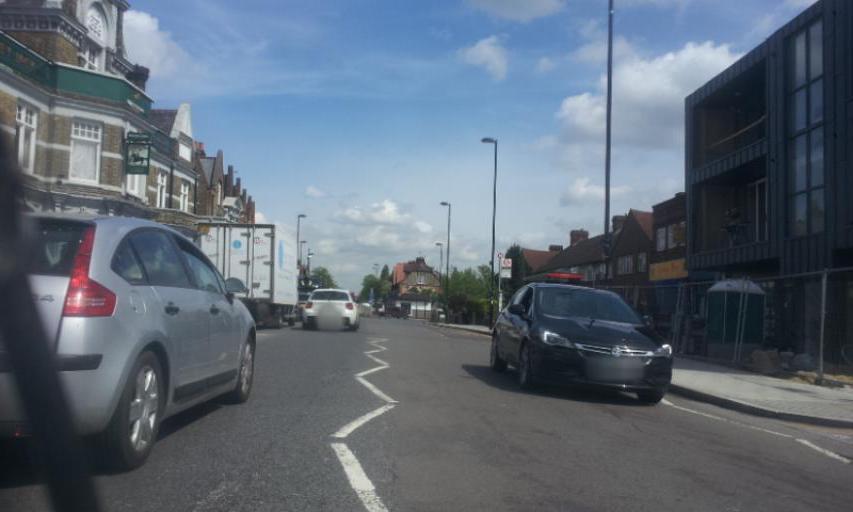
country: GB
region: England
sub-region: Greater London
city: Catford
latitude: 51.4531
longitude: -0.0385
